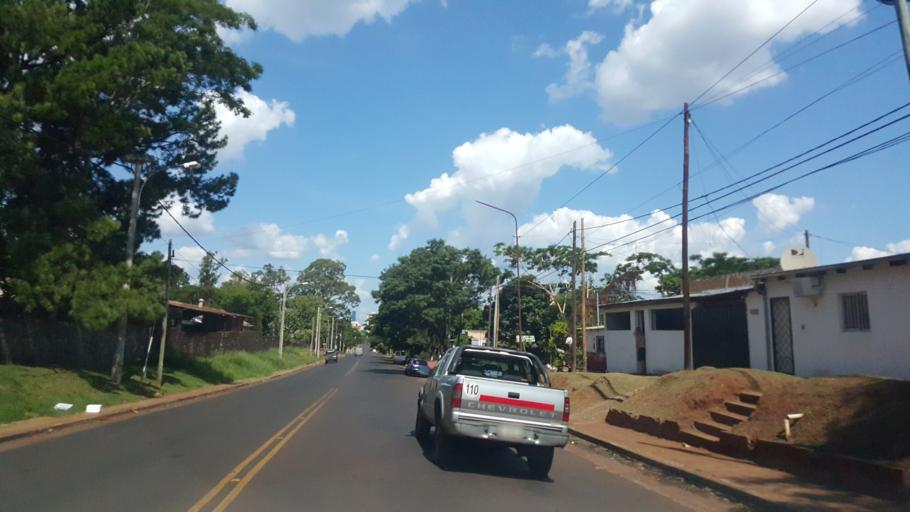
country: AR
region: Misiones
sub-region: Departamento de Capital
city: Posadas
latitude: -27.3653
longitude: -55.9187
